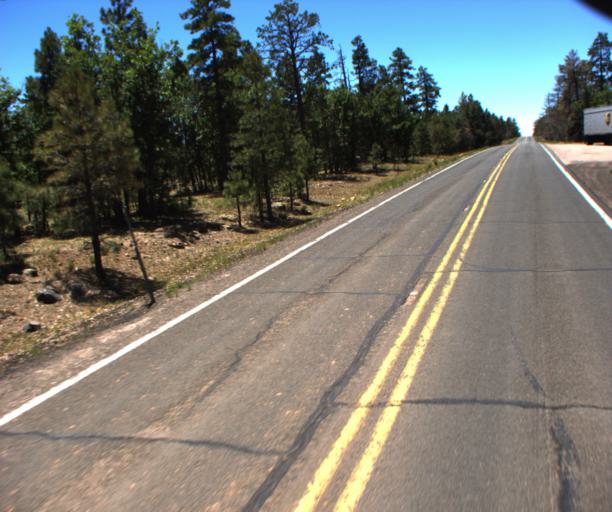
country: US
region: Arizona
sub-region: Gila County
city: Pine
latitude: 34.5911
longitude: -111.2512
